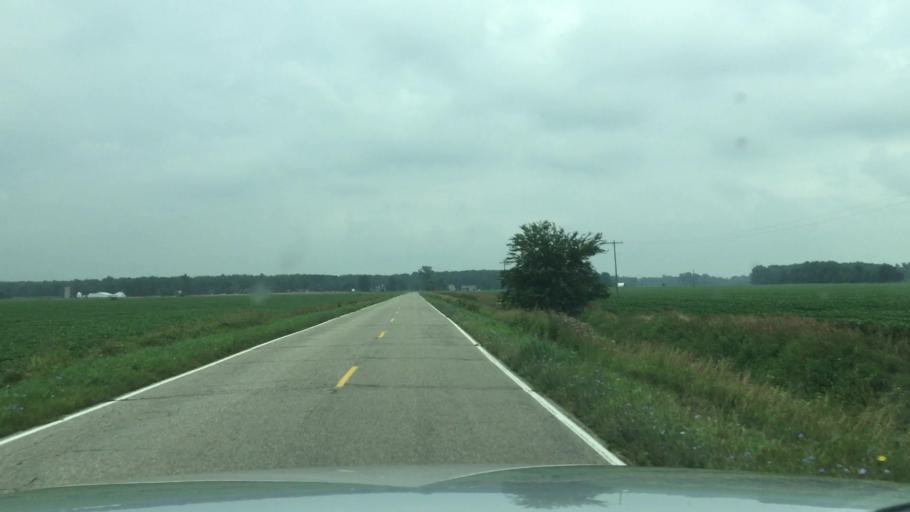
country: US
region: Michigan
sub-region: Shiawassee County
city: New Haven
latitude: 43.0674
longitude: -84.2261
